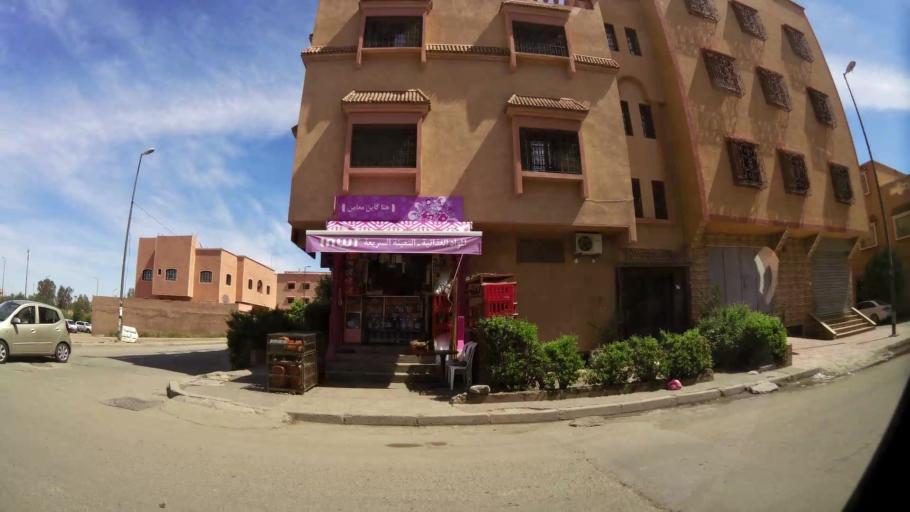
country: MA
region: Marrakech-Tensift-Al Haouz
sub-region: Marrakech
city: Marrakesh
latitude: 31.6618
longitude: -7.9877
